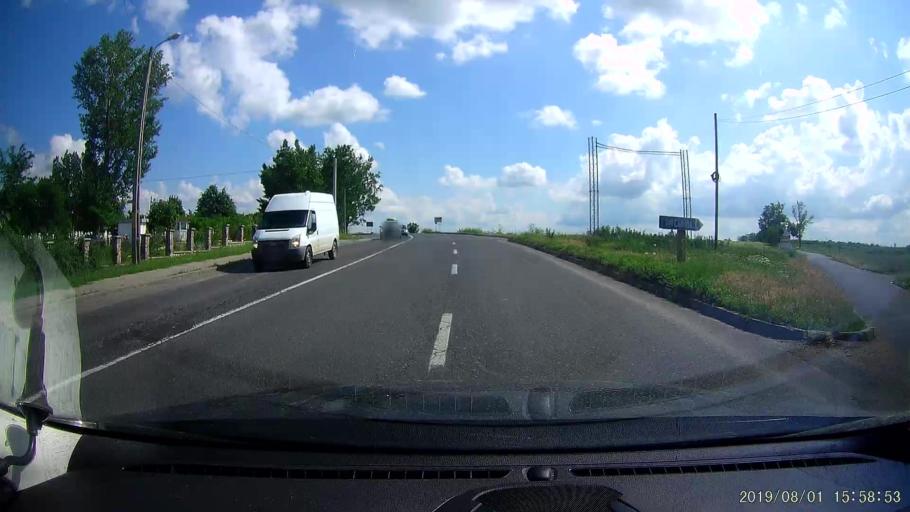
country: RO
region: Ialomita
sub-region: Comuna Slobozia
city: Slobozia
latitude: 44.5590
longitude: 27.3810
